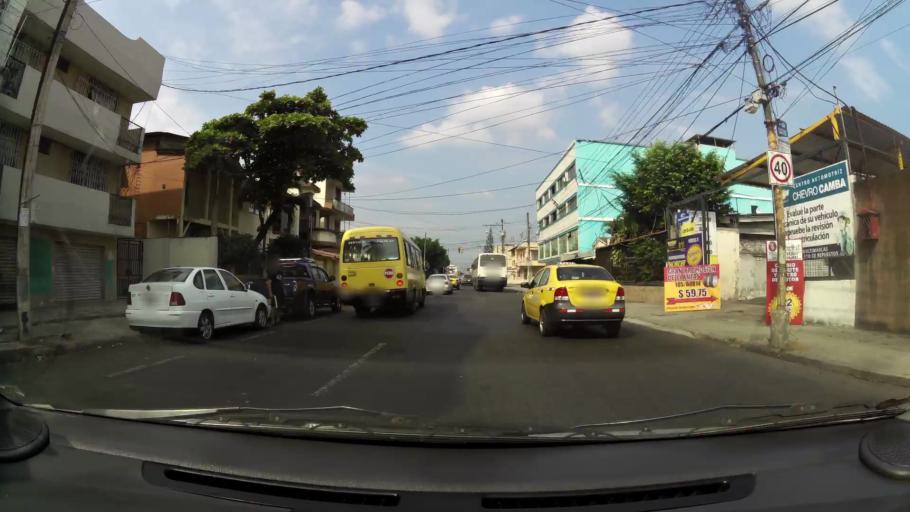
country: EC
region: Guayas
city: Guayaquil
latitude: -2.1917
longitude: -79.8976
